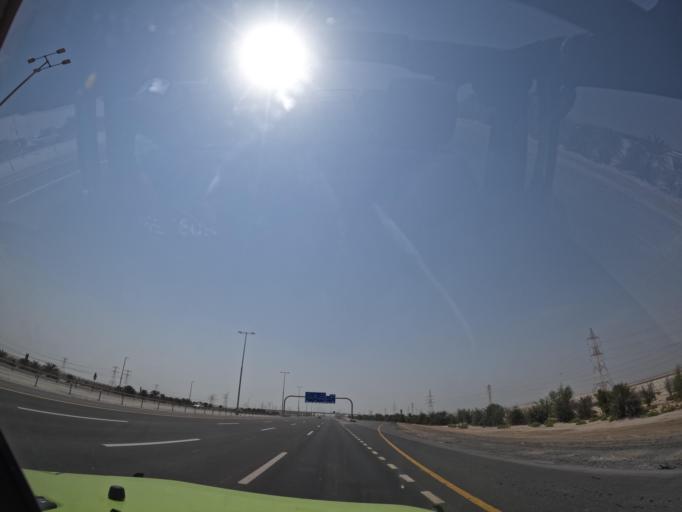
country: AE
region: Abu Dhabi
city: Abu Dhabi
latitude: 24.1692
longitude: 54.3606
